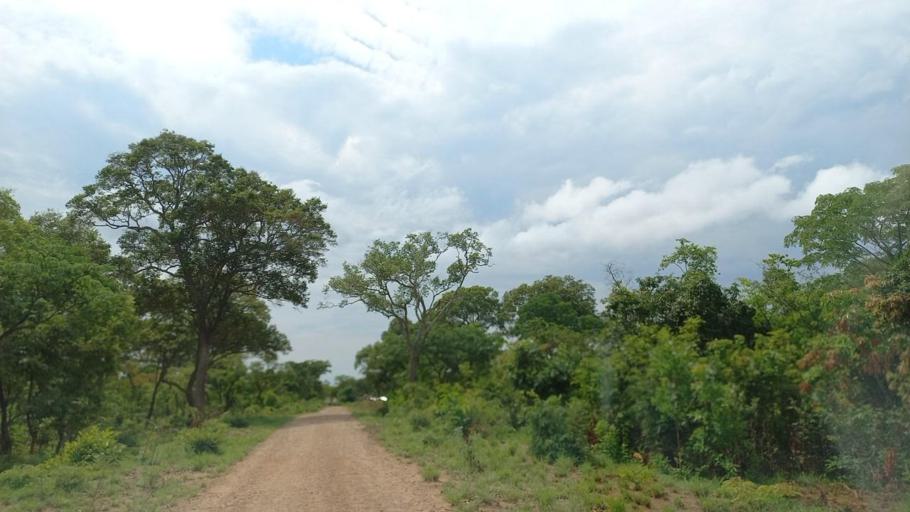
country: ZM
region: North-Western
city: Kalengwa
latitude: -13.4619
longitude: 25.0070
